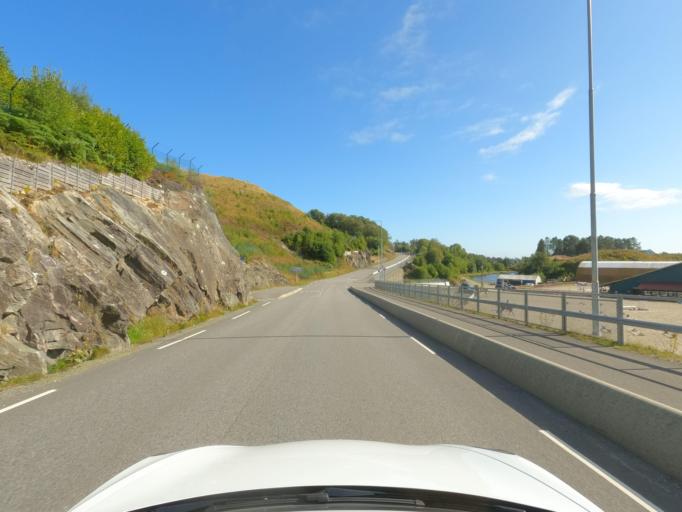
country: NO
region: Hordaland
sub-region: Bergen
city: Ytrebygda
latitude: 60.2801
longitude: 5.2190
